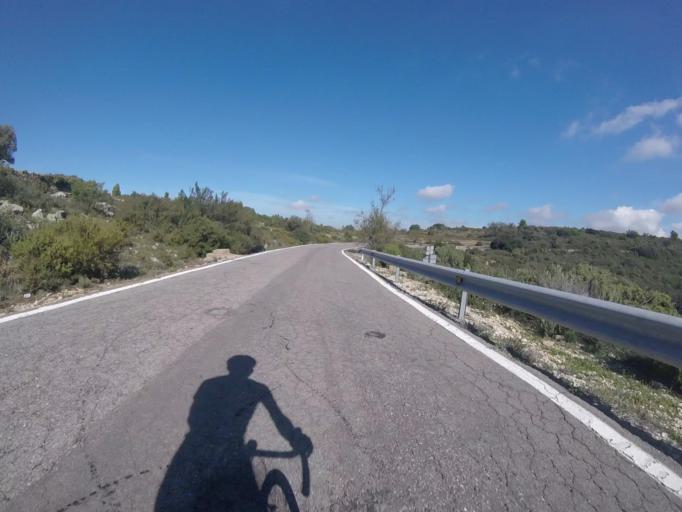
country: ES
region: Valencia
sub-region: Provincia de Castello
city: Albocasser
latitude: 40.3333
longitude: 0.0373
